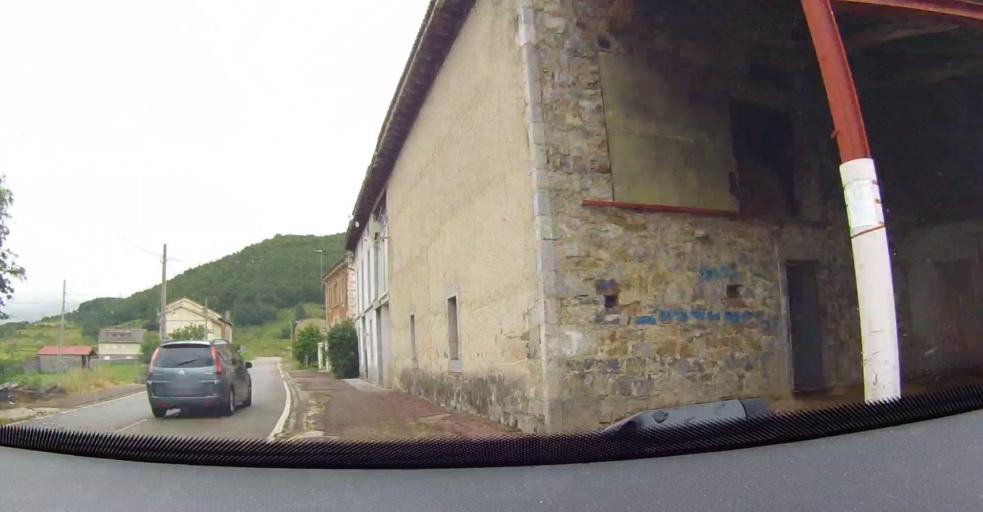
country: ES
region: Castille and Leon
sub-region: Provincia de Leon
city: Acebedo
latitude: 43.0632
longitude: -5.1380
